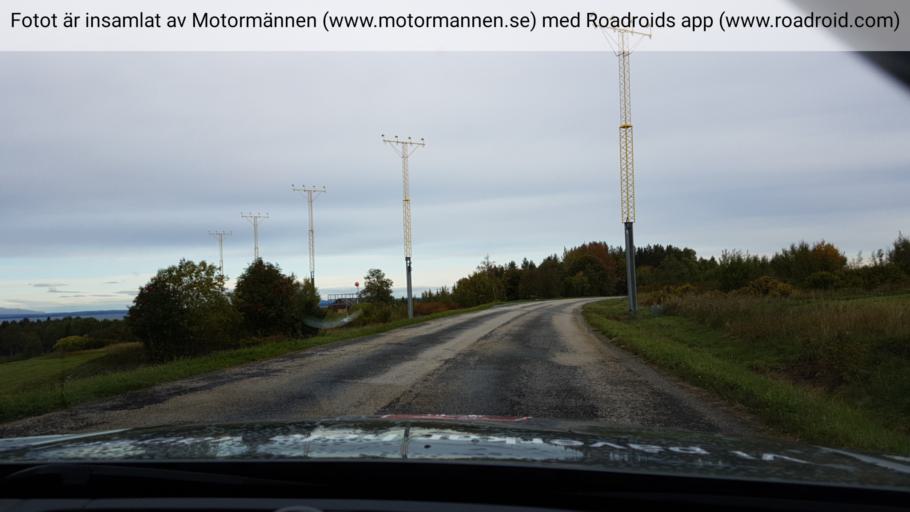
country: SE
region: Jaemtland
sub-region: Krokoms Kommun
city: Krokom
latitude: 63.2007
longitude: 14.4693
